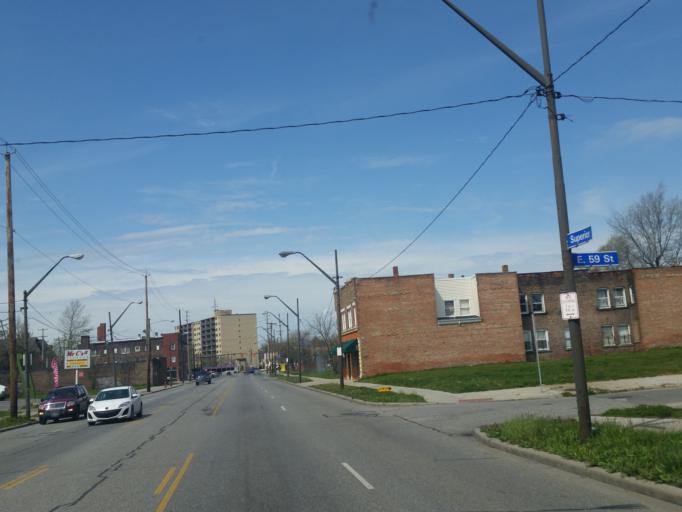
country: US
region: Ohio
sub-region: Cuyahoga County
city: Bratenahl
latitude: 41.5182
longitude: -81.6491
